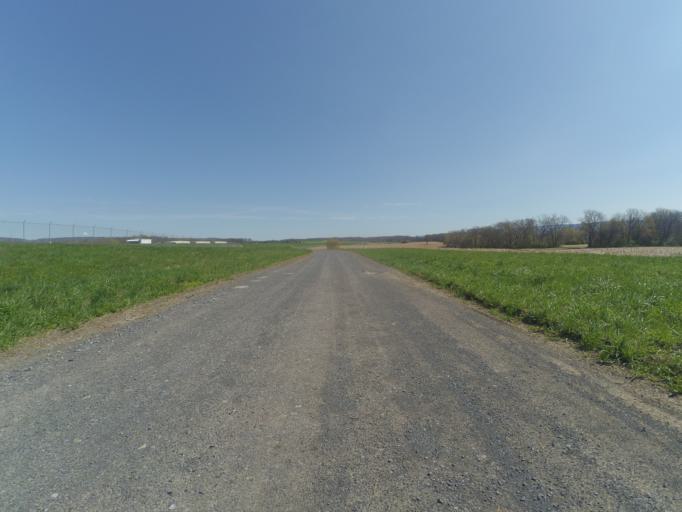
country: US
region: Pennsylvania
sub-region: Centre County
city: Houserville
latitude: 40.8477
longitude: -77.8482
